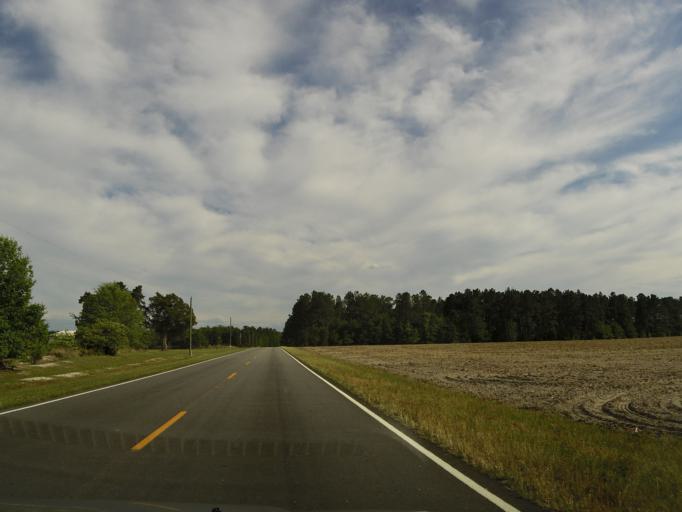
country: US
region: South Carolina
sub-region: Allendale County
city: Fairfax
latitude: 33.0210
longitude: -81.2180
